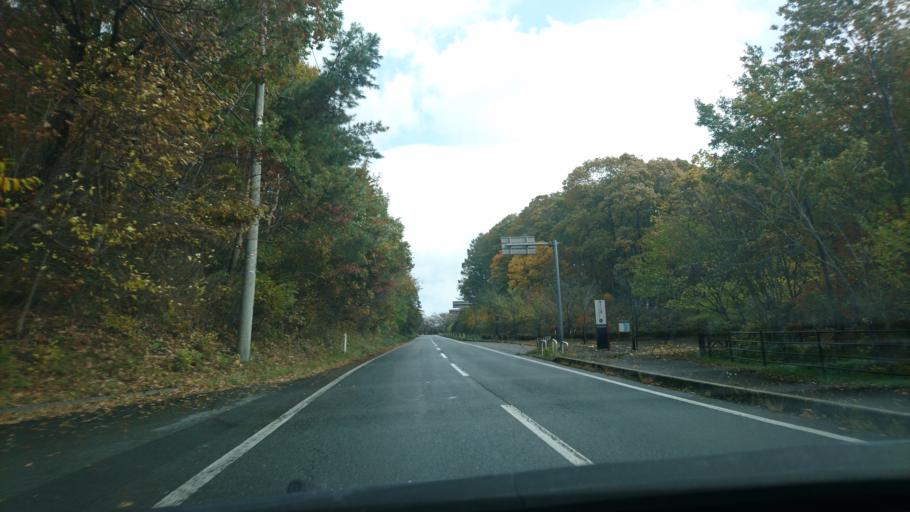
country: JP
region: Iwate
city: Shizukuishi
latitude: 39.6845
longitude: 141.0183
